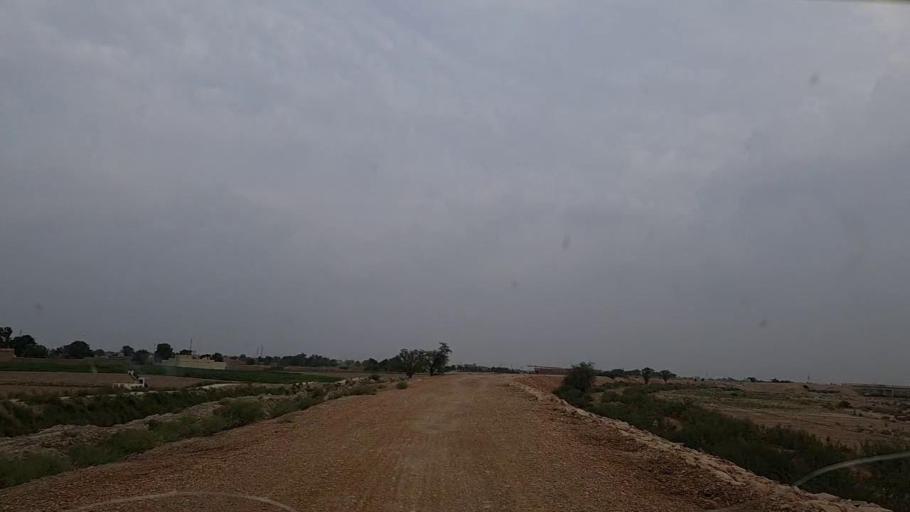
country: PK
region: Sindh
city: Johi
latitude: 26.7020
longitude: 67.5977
